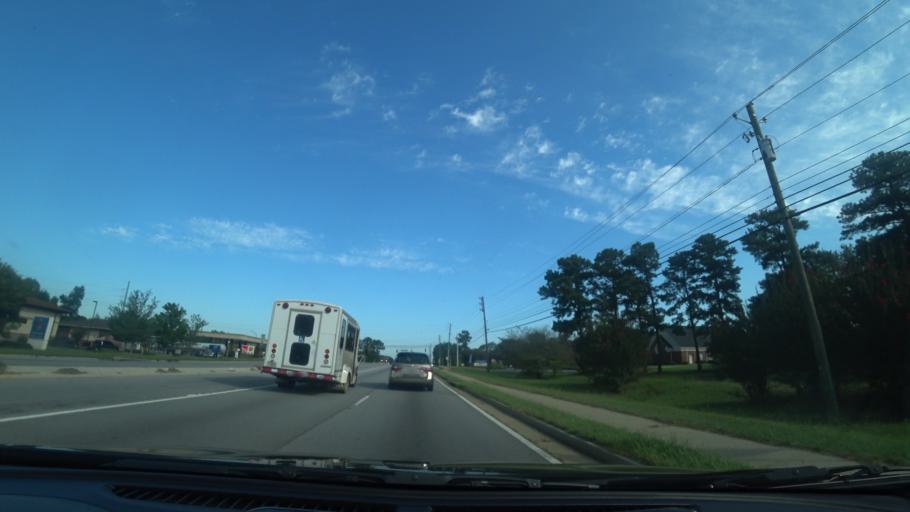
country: US
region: Georgia
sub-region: Gwinnett County
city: Grayson
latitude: 33.9110
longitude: -83.9689
